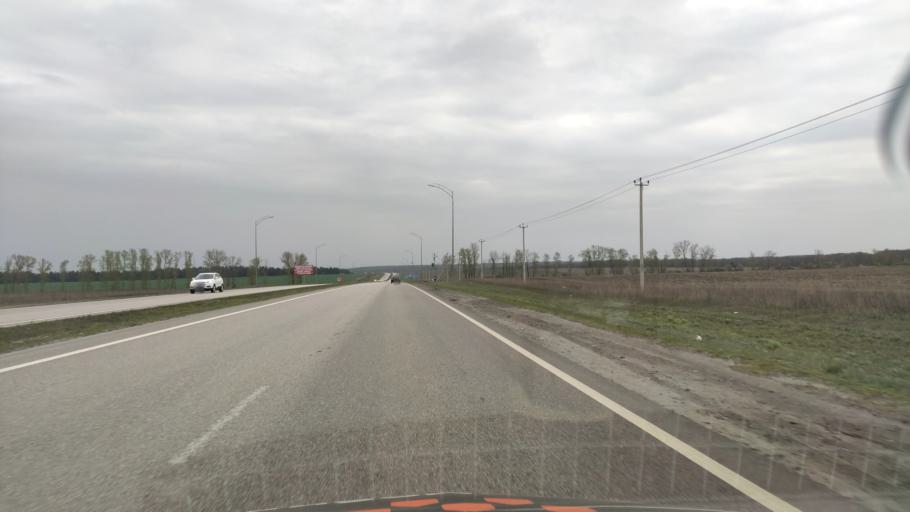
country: RU
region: Belgorod
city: Staryy Oskol
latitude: 51.3866
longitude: 37.8614
